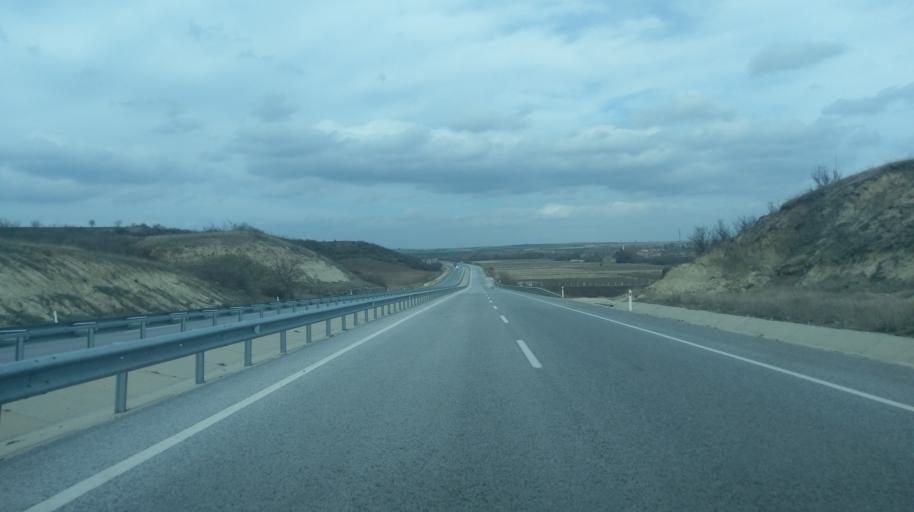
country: TR
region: Edirne
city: Kircasalih
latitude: 41.4462
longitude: 26.8187
